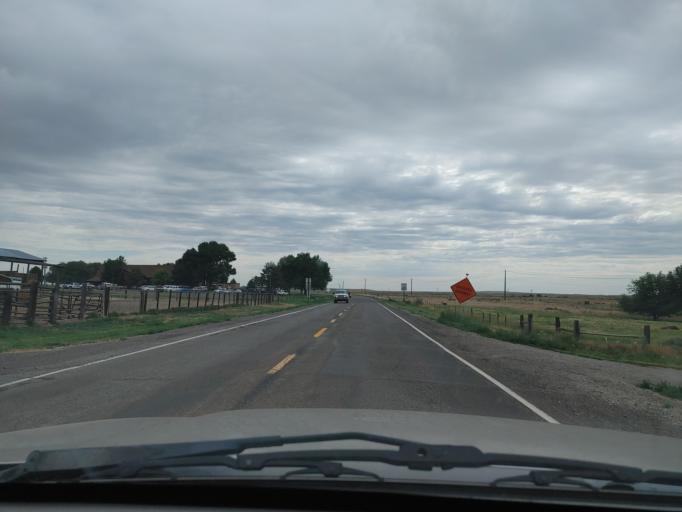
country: US
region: Idaho
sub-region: Lincoln County
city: Shoshone
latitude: 43.0493
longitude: -114.1505
